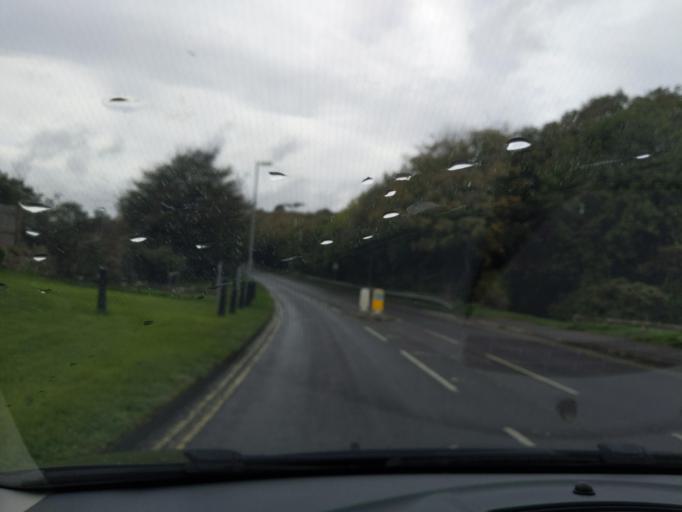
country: GB
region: England
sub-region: Cornwall
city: Padstow
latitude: 50.5399
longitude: -4.9427
